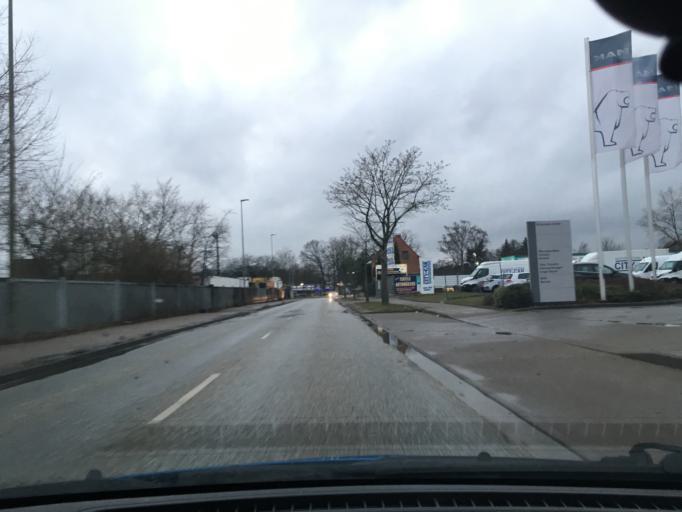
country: DE
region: Schleswig-Holstein
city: Geesthacht
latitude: 53.4325
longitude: 10.3574
